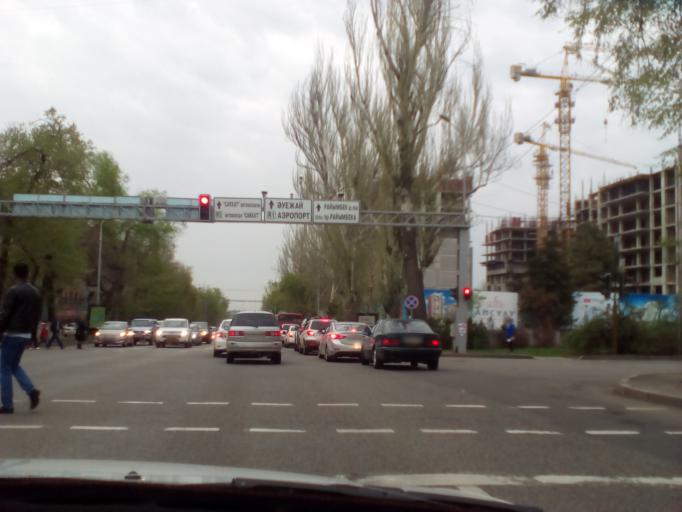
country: KZ
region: Almaty Qalasy
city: Almaty
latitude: 43.2671
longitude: 76.9452
